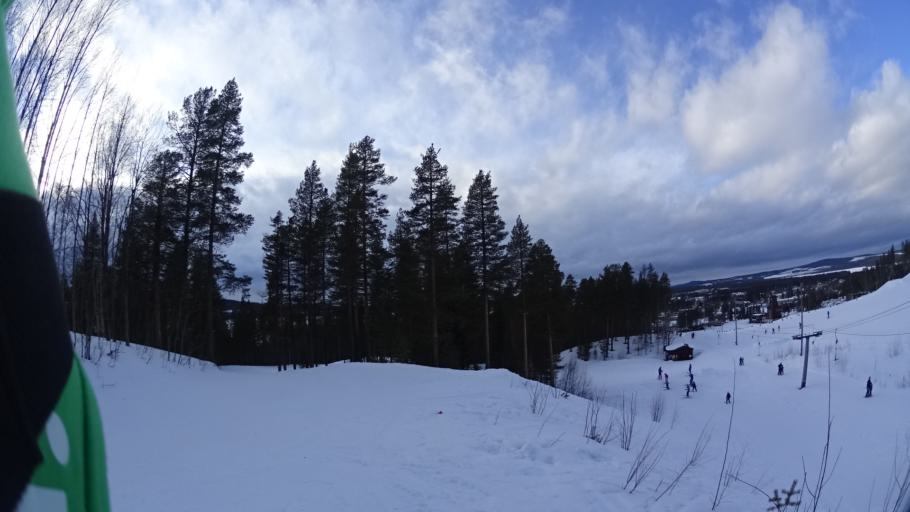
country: SE
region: Vaesterbotten
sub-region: Mala Kommun
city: Mala
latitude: 65.1790
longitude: 18.7550
